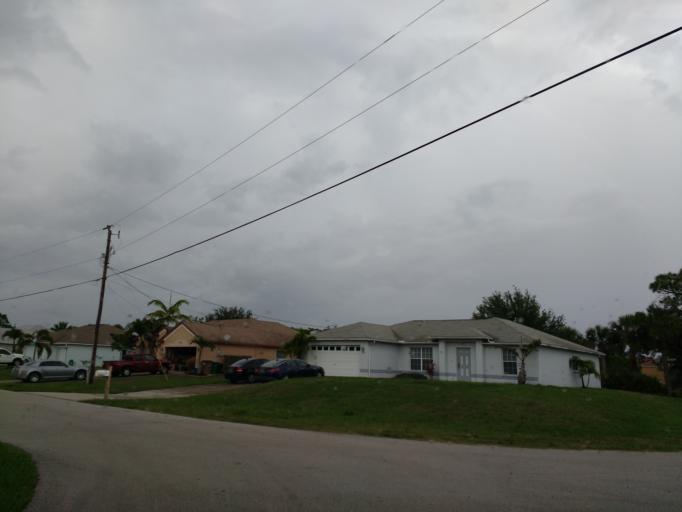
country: US
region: Florida
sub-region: Lee County
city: Cape Coral
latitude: 26.6109
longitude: -82.0199
